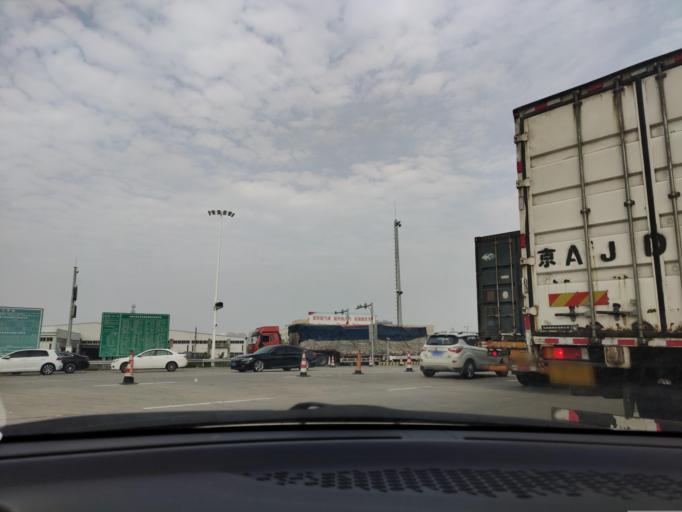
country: CN
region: Shandong Sheng
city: Fuxin
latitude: 37.5299
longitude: 121.2158
